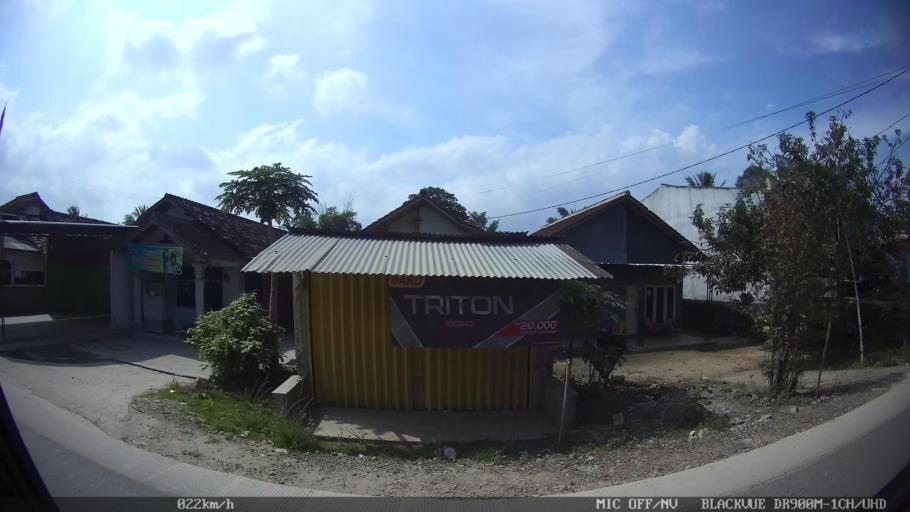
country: ID
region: Lampung
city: Kedaton
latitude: -5.3511
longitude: 105.2639
